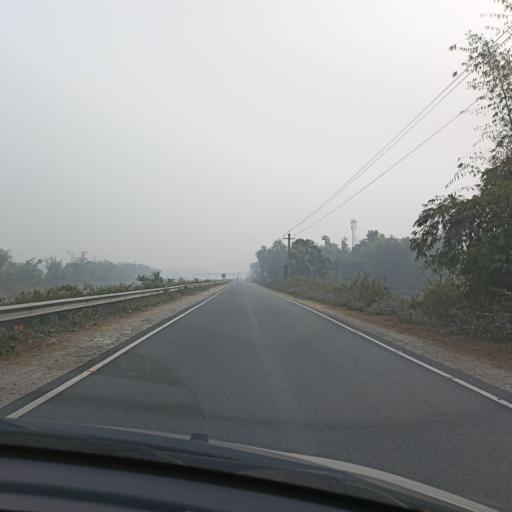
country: IN
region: West Bengal
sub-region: Darjiling
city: Shiliguri
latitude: 26.6805
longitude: 88.5561
